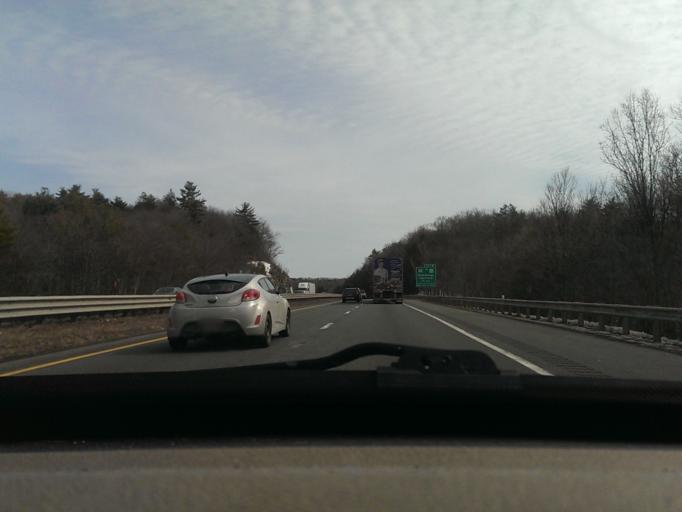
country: US
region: Massachusetts
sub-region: Worcester County
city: Sturbridge
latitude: 42.1321
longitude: -72.0737
